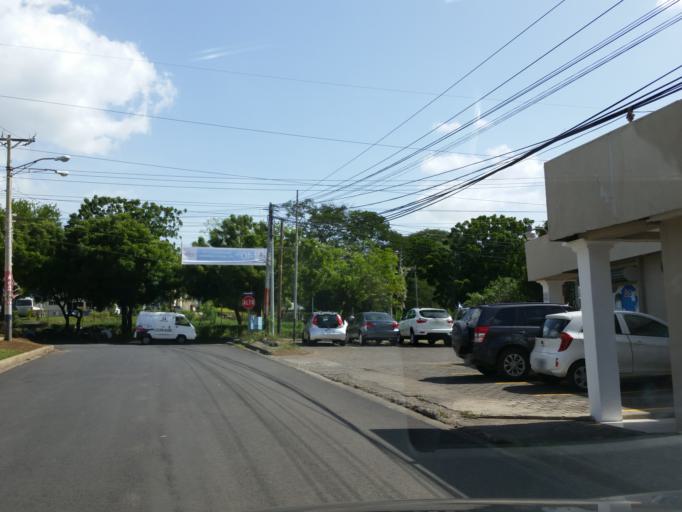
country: NI
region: Managua
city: Managua
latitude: 12.1132
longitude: -86.2698
